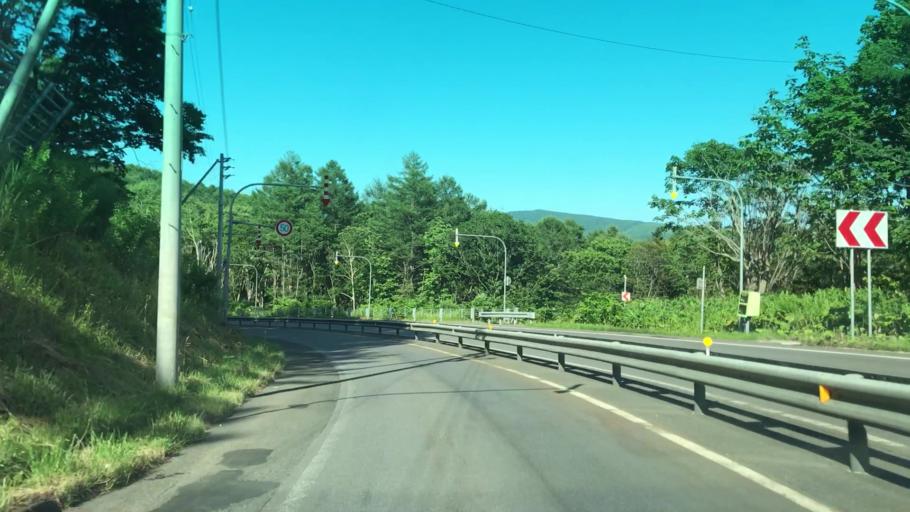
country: JP
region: Hokkaido
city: Yoichi
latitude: 43.0623
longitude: 140.6929
